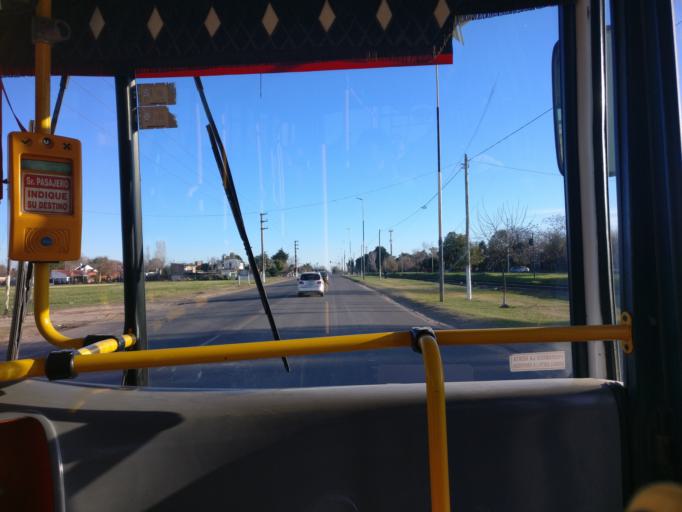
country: AR
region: Buenos Aires
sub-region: Partido de Ezeiza
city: Ezeiza
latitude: -34.8955
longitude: -58.5754
